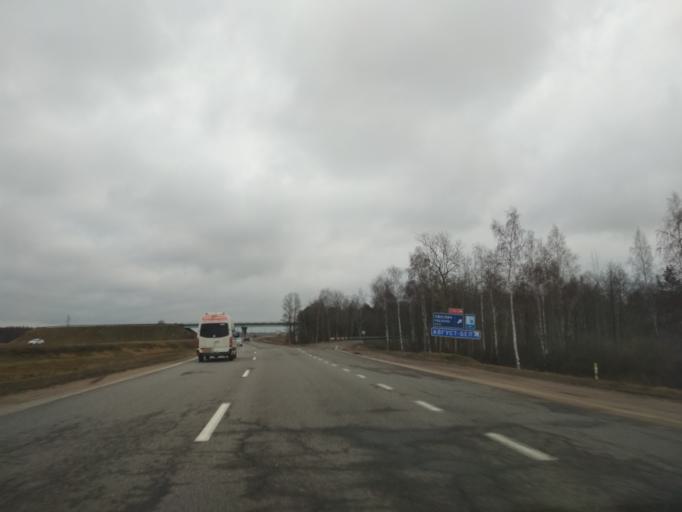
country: BY
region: Minsk
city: Dukora
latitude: 53.6613
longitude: 27.9434
